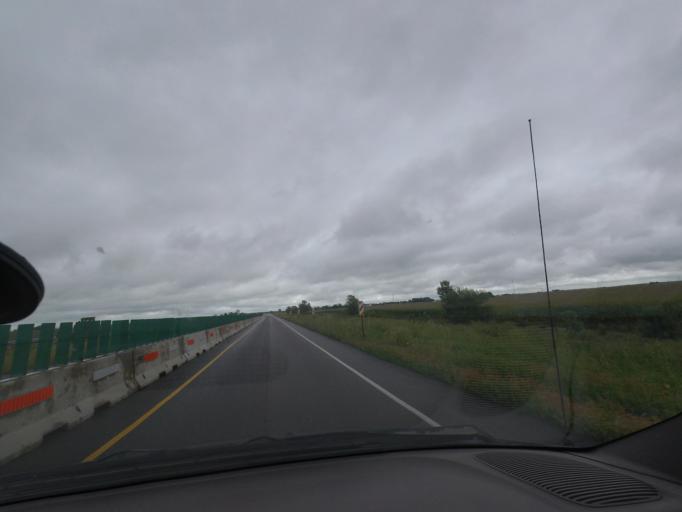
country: US
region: Illinois
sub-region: Piatt County
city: Cerro Gordo
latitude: 40.0154
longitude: -88.7566
